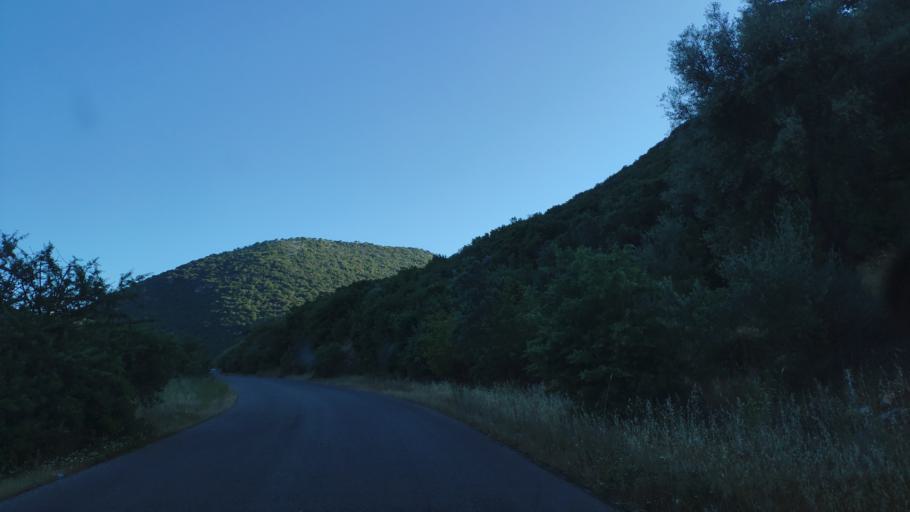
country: GR
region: West Greece
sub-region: Nomos Aitolias kai Akarnanias
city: Fitiai
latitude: 38.6154
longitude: 21.1413
